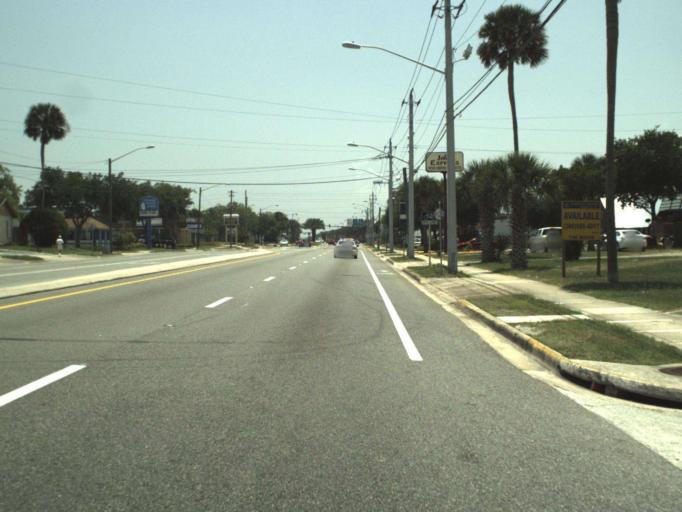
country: US
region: Florida
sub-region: Volusia County
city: South Daytona
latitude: 29.1869
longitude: -81.0101
